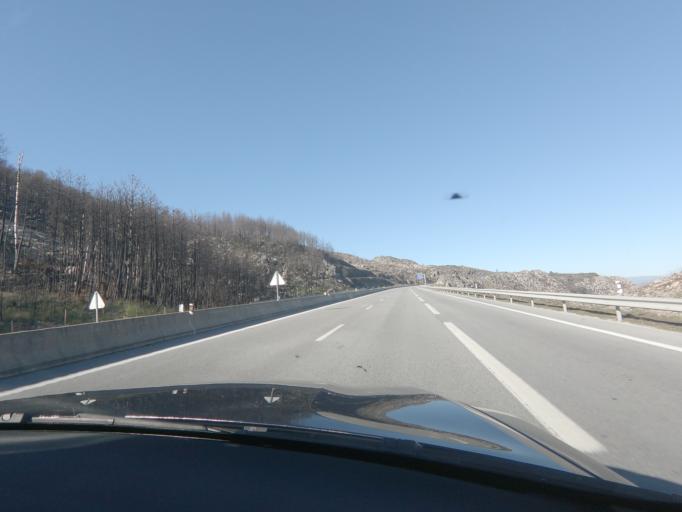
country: PT
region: Viseu
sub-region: Vouzela
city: Vouzela
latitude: 40.6727
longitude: -8.0763
